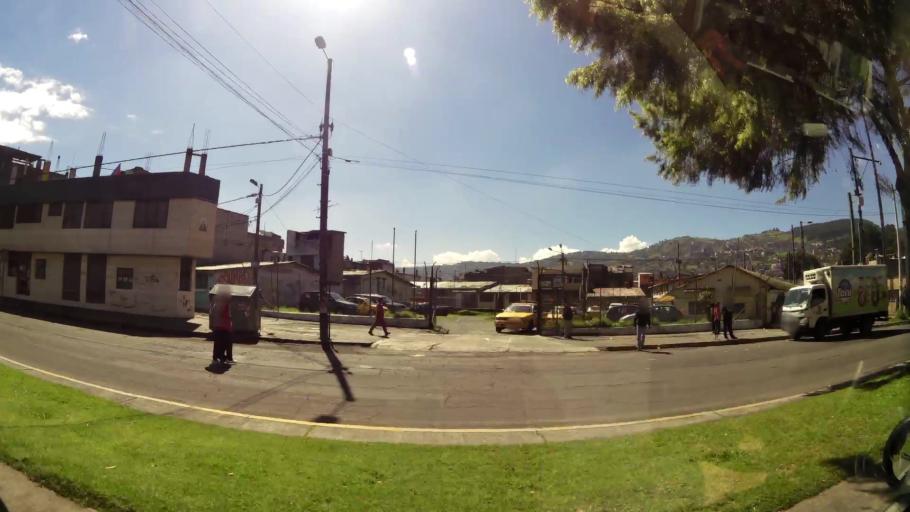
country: EC
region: Pichincha
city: Quito
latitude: -0.2572
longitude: -78.5294
